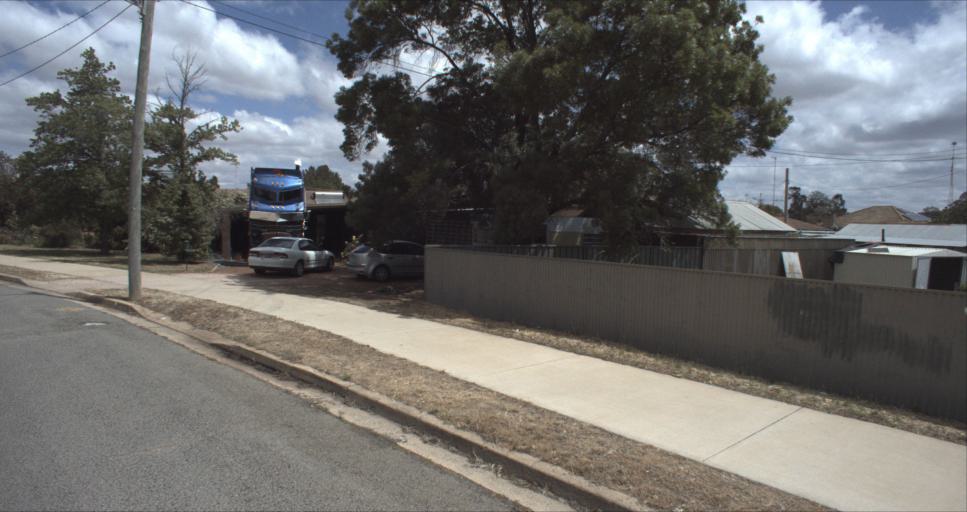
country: AU
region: New South Wales
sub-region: Leeton
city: Leeton
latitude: -34.5578
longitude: 146.3987
